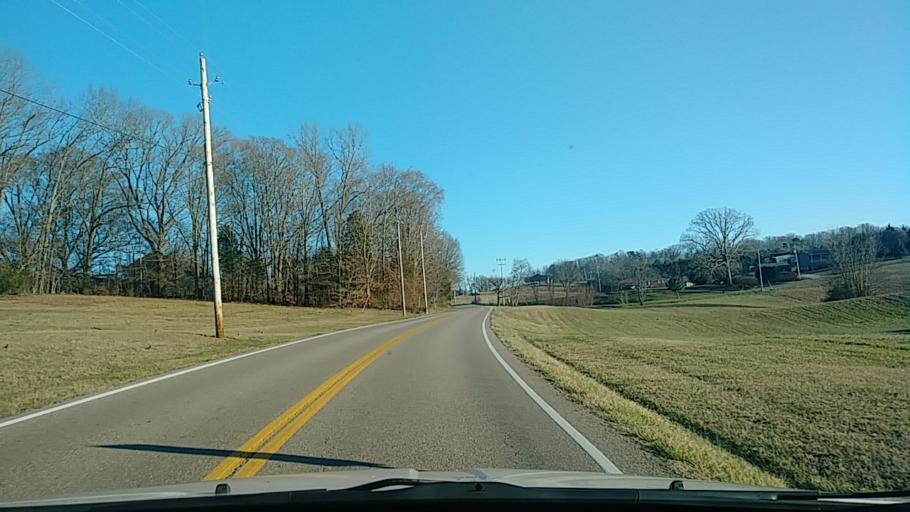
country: US
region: Tennessee
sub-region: Hamblen County
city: Morristown
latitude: 36.2047
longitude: -83.4060
